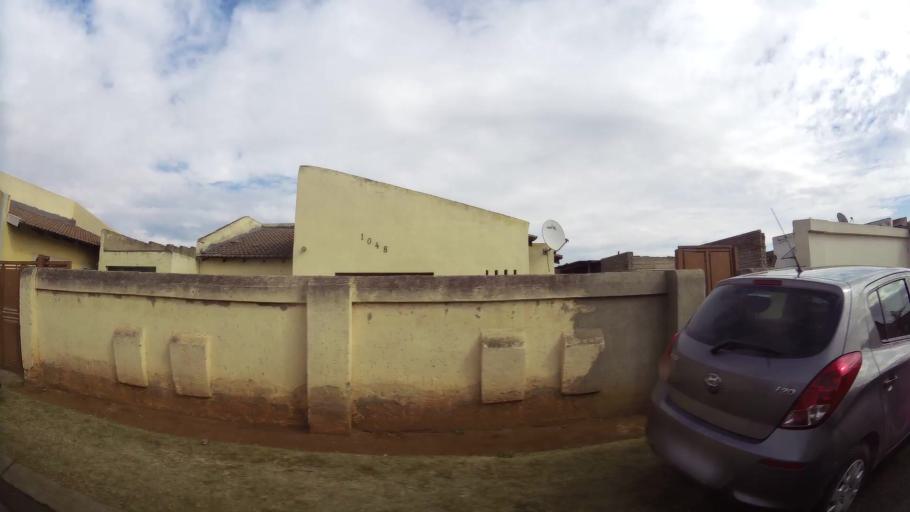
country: ZA
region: Gauteng
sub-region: Ekurhuleni Metropolitan Municipality
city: Germiston
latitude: -26.3256
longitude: 28.1785
